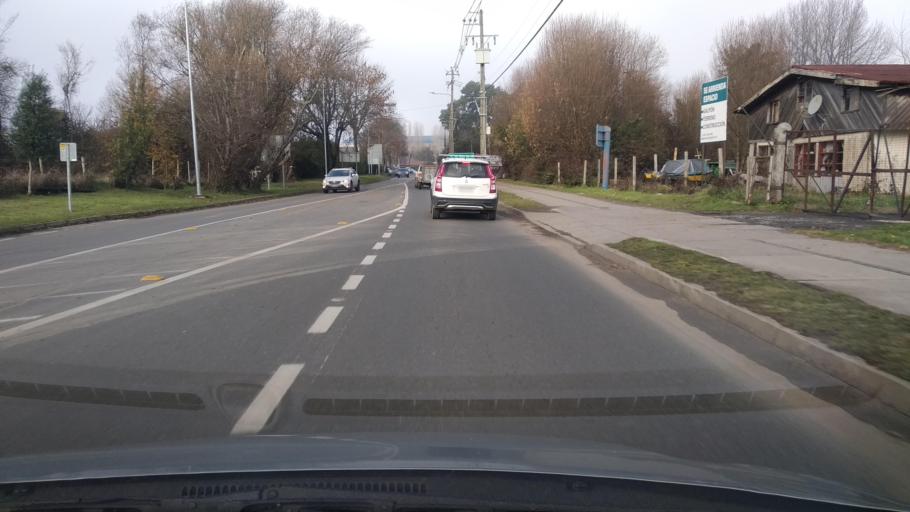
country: CL
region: Los Rios
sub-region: Provincia de Valdivia
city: Valdivia
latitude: -39.8047
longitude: -73.2414
